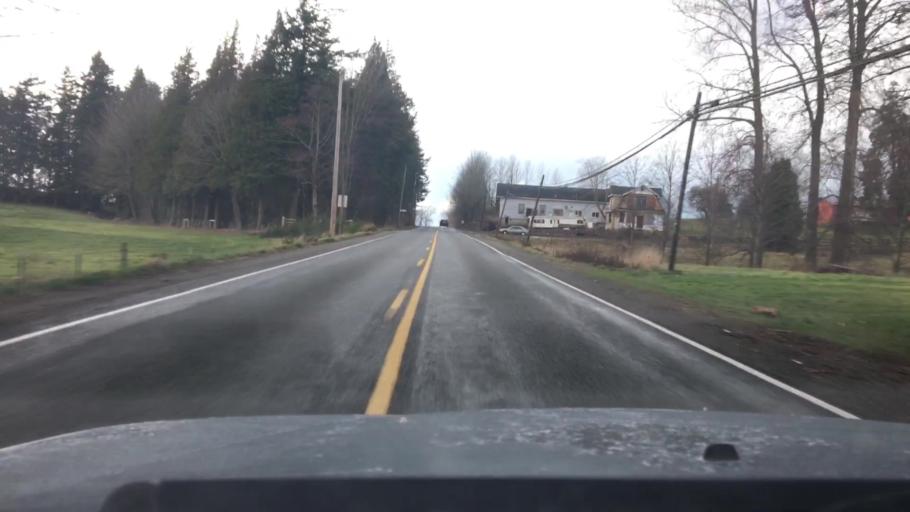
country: US
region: Washington
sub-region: Whatcom County
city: Ferndale
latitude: 48.8484
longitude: -122.6701
